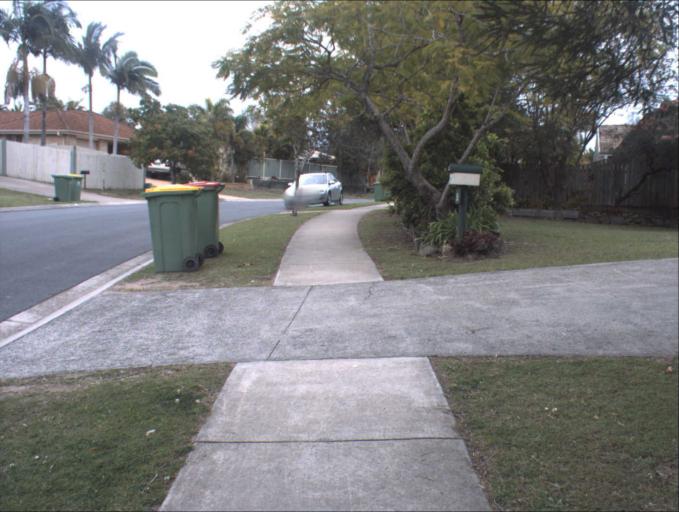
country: AU
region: Queensland
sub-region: Logan
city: Park Ridge South
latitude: -27.6711
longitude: 153.0484
